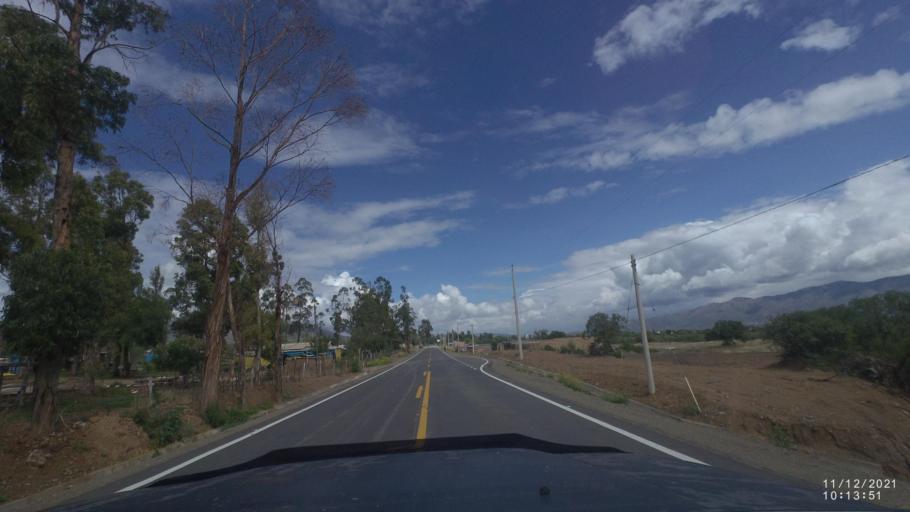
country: BO
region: Cochabamba
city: Tarata
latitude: -17.6199
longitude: -66.0132
